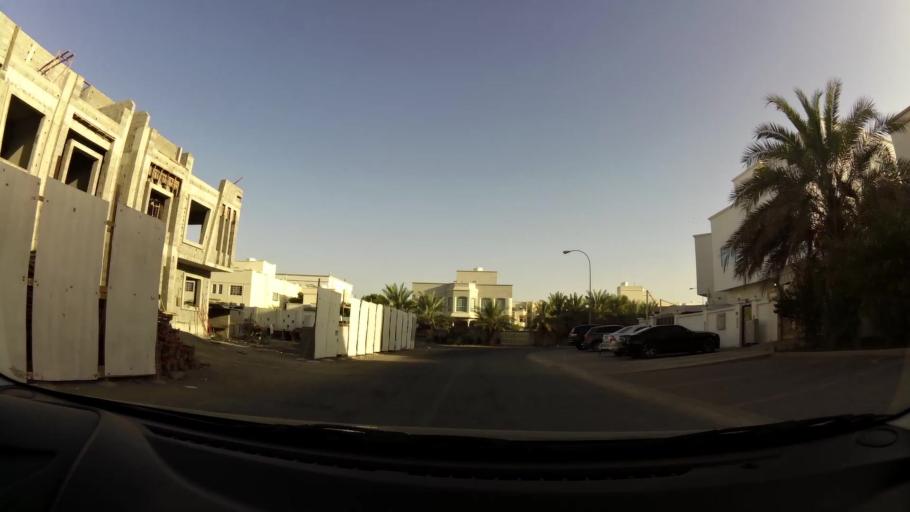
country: OM
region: Muhafazat Masqat
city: As Sib al Jadidah
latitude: 23.6115
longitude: 58.2280
